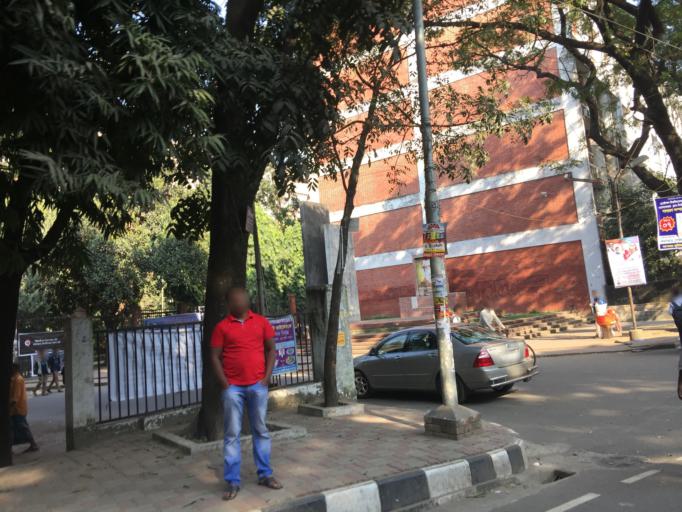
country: BD
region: Dhaka
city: Azimpur
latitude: 23.7260
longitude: 90.3915
